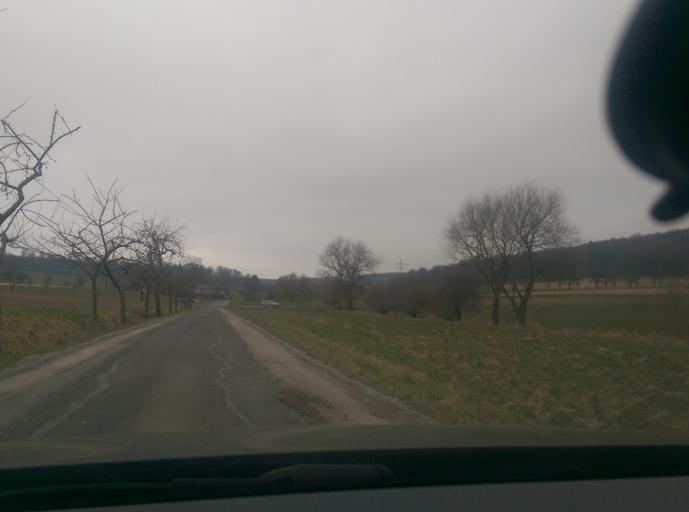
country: DE
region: Lower Saxony
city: Hameln
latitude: 52.1294
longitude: 9.3873
